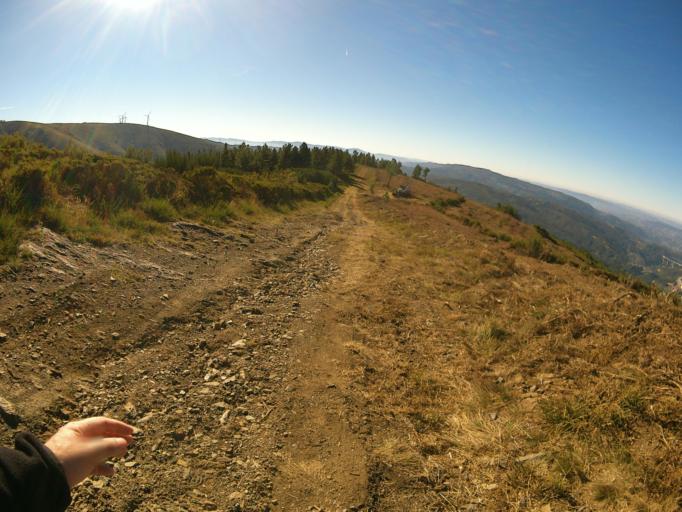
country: PT
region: Vila Real
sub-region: Mesao Frio
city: Mesao Frio
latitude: 41.2486
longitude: -7.9204
